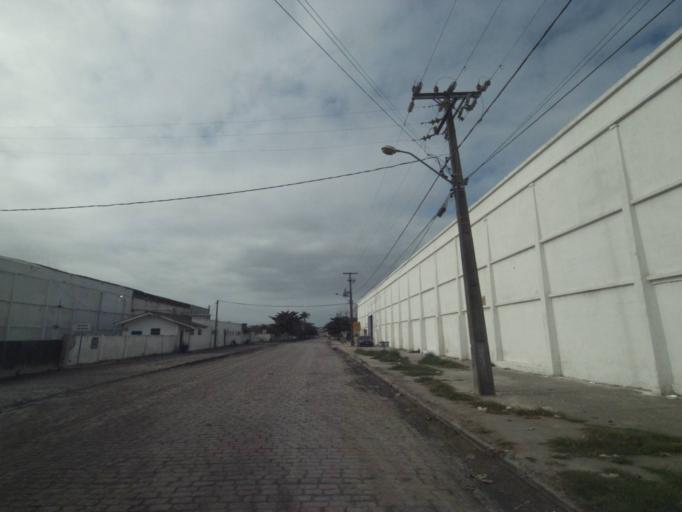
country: BR
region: Parana
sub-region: Paranagua
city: Paranagua
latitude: -25.5089
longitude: -48.5289
